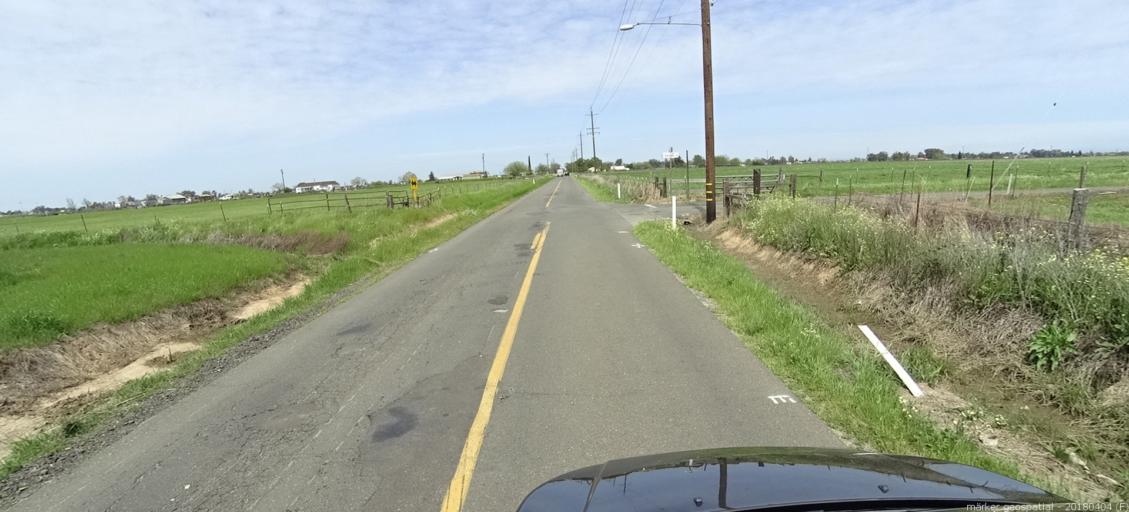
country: US
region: California
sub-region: Sacramento County
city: Herald
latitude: 38.2769
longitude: -121.2642
